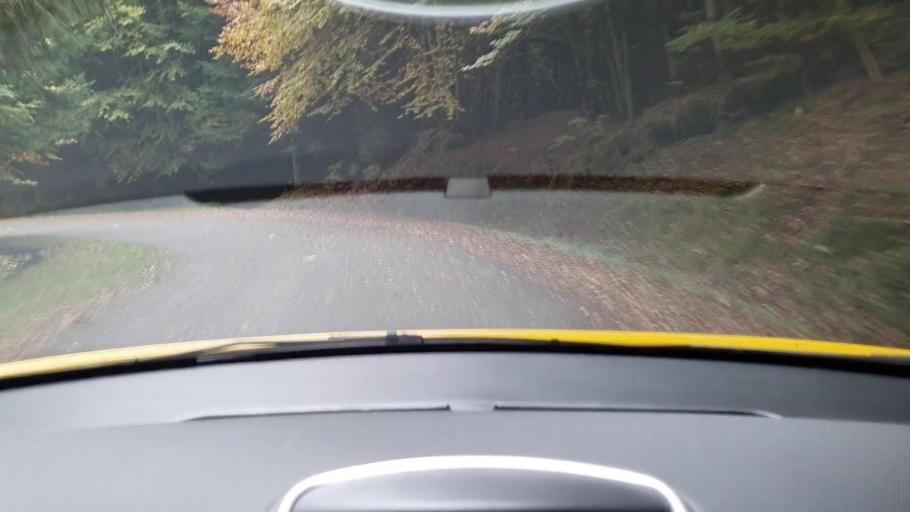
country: FR
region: Languedoc-Roussillon
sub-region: Departement de la Lozere
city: Meyrueis
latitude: 44.0881
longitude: 3.4543
